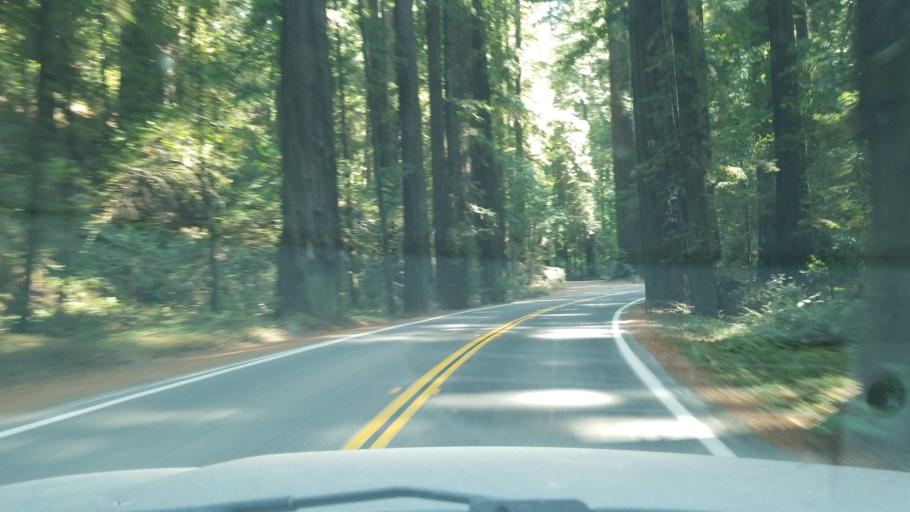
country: US
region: California
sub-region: Humboldt County
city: Redway
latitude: 40.2553
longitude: -123.8211
